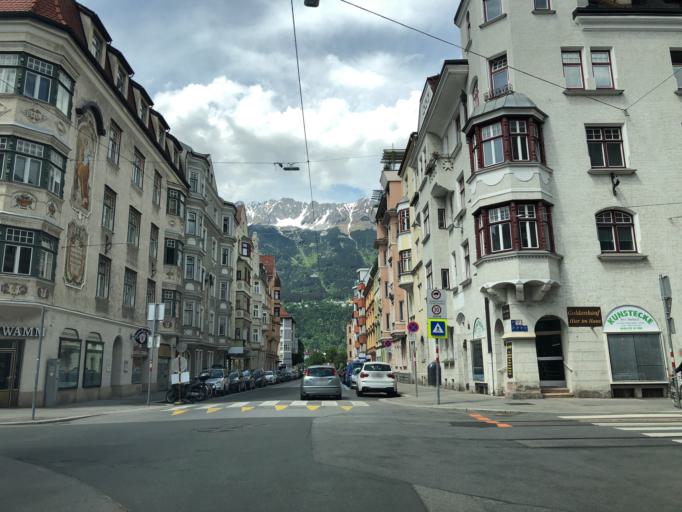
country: AT
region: Tyrol
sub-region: Innsbruck Stadt
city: Innsbruck
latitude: 47.2649
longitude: 11.4099
